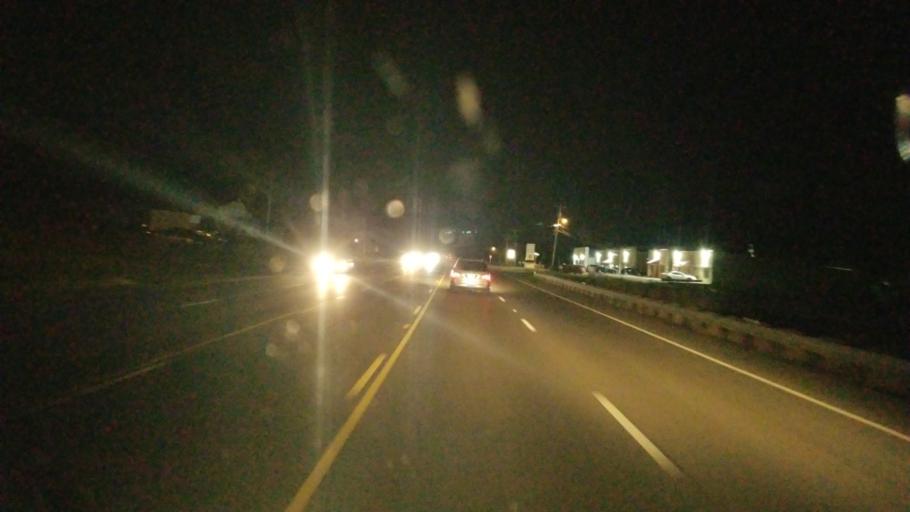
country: US
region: Ohio
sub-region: Pike County
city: Waverly
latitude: 39.1545
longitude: -82.9768
